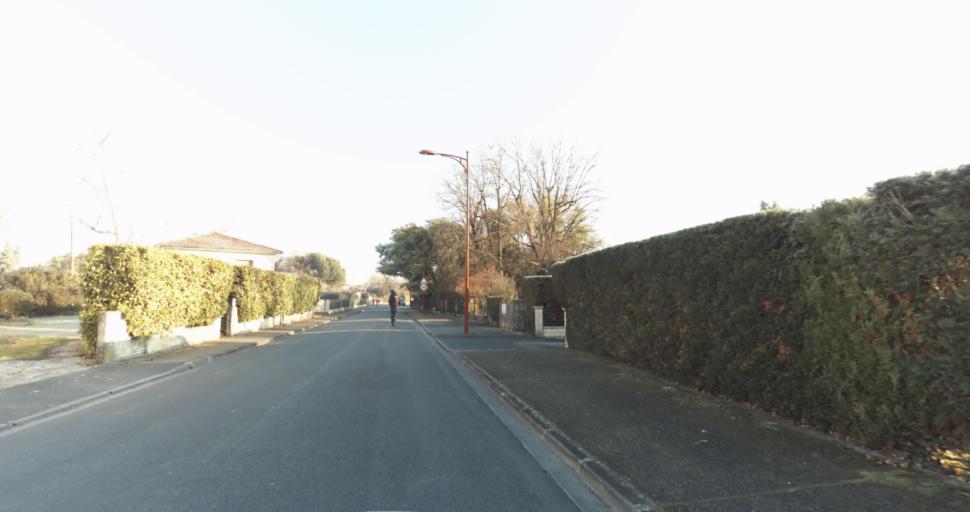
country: FR
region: Aquitaine
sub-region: Departement de la Gironde
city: Carbon-Blanc
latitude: 44.9061
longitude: -0.4999
